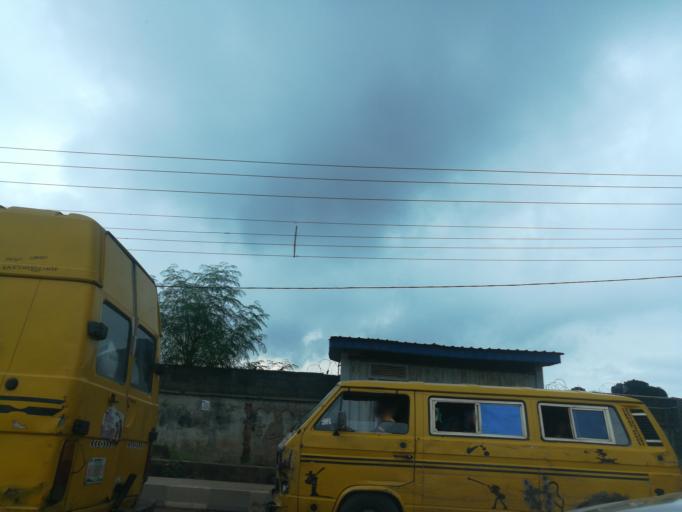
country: NG
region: Lagos
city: Ikeja
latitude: 6.5979
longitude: 3.3345
